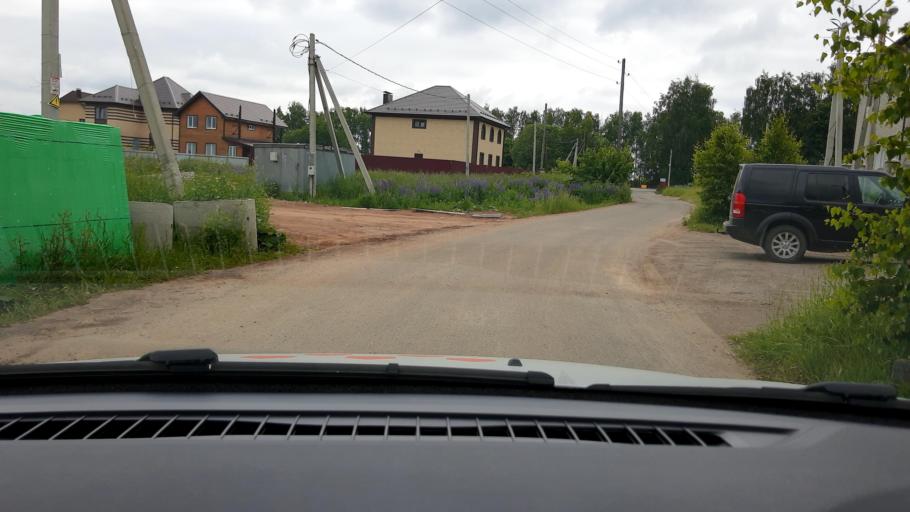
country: RU
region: Nizjnij Novgorod
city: Nizhniy Novgorod
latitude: 56.2154
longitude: 43.9660
